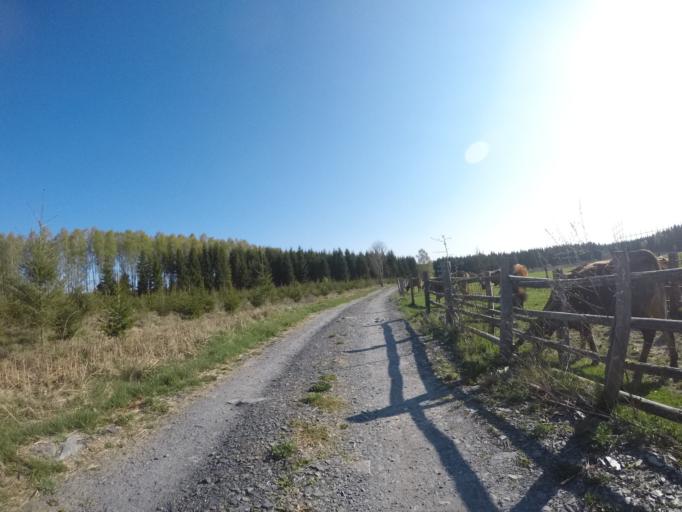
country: BE
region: Wallonia
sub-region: Province du Luxembourg
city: Leglise
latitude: 49.7802
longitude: 5.5715
